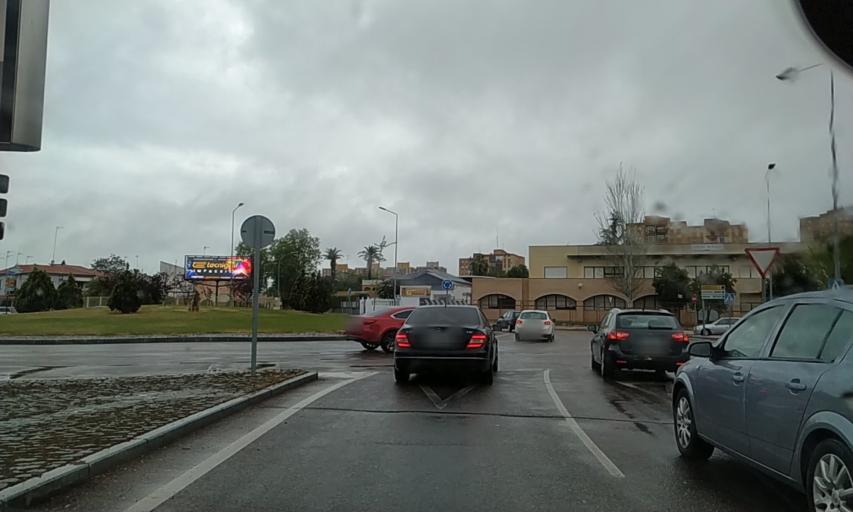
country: ES
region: Extremadura
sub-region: Provincia de Badajoz
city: Badajoz
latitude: 38.8836
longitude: -6.9851
